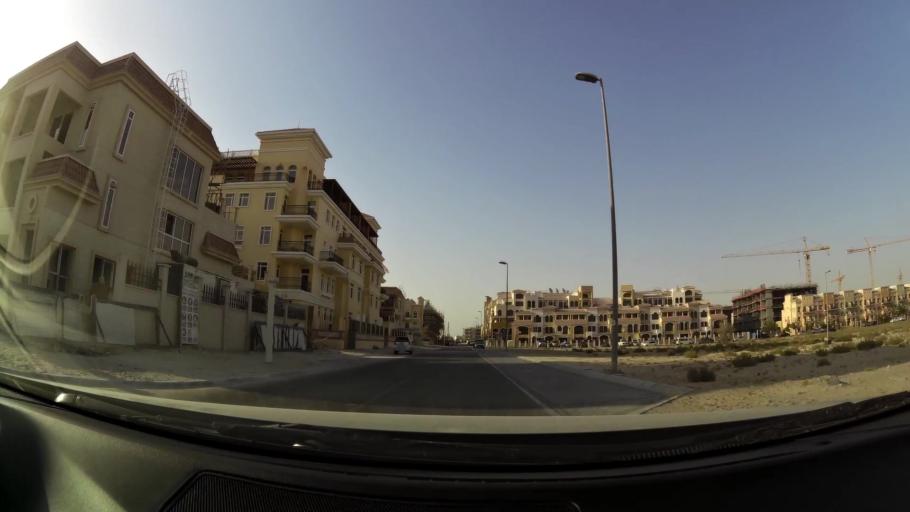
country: AE
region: Dubai
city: Dubai
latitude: 25.0644
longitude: 55.2120
